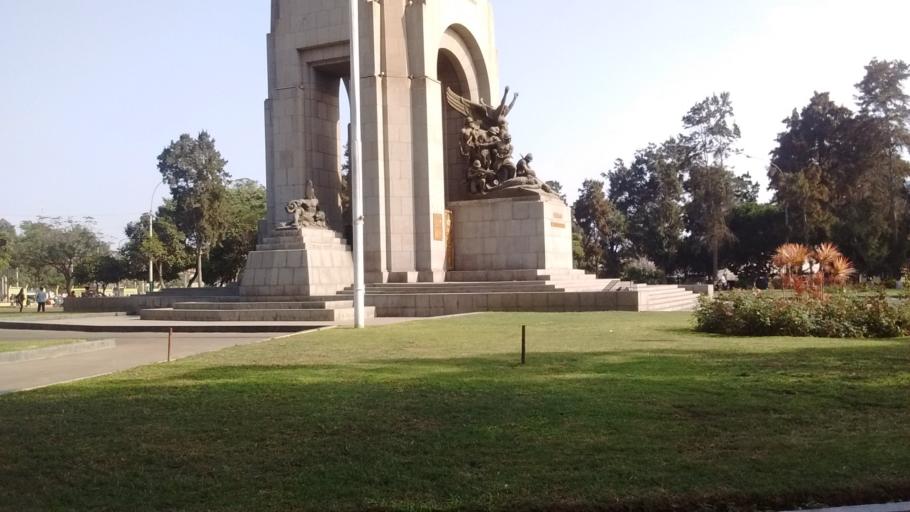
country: PE
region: Lima
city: Lima
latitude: -12.0679
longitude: -77.0411
